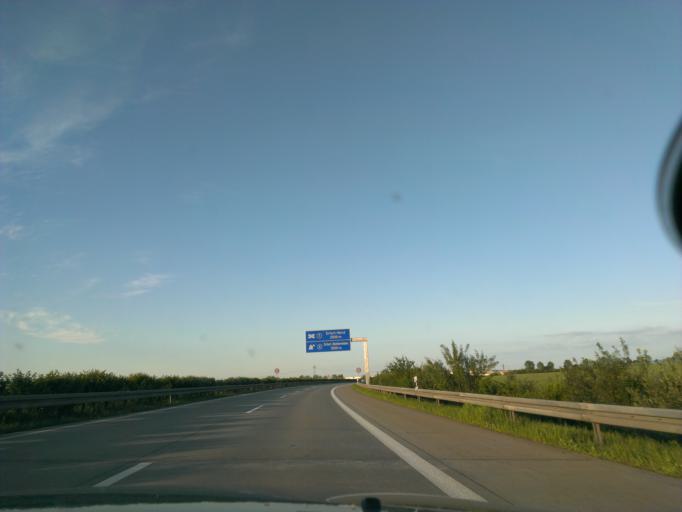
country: DE
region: Thuringia
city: Noda
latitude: 51.0387
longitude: 11.0193
